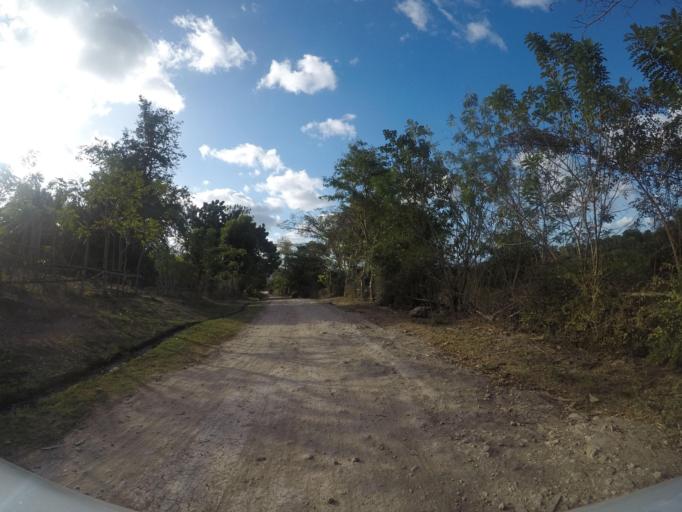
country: TL
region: Lautem
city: Lospalos
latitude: -8.4323
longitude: 126.8484
